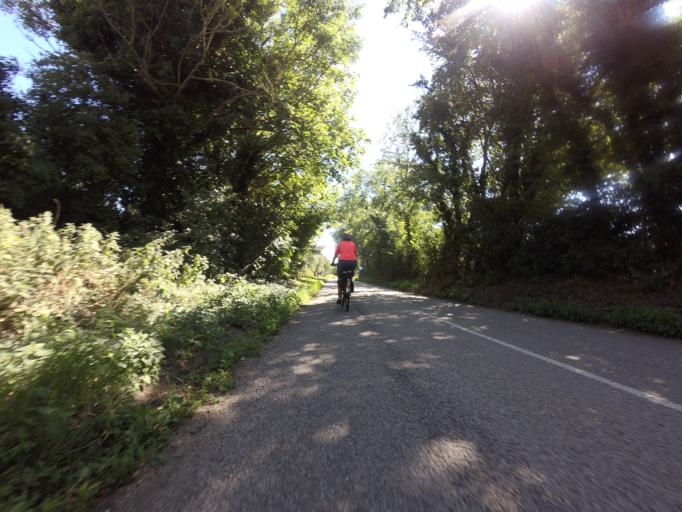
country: GB
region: England
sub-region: Kent
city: Birchington-on-Sea
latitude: 51.3340
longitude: 1.3221
